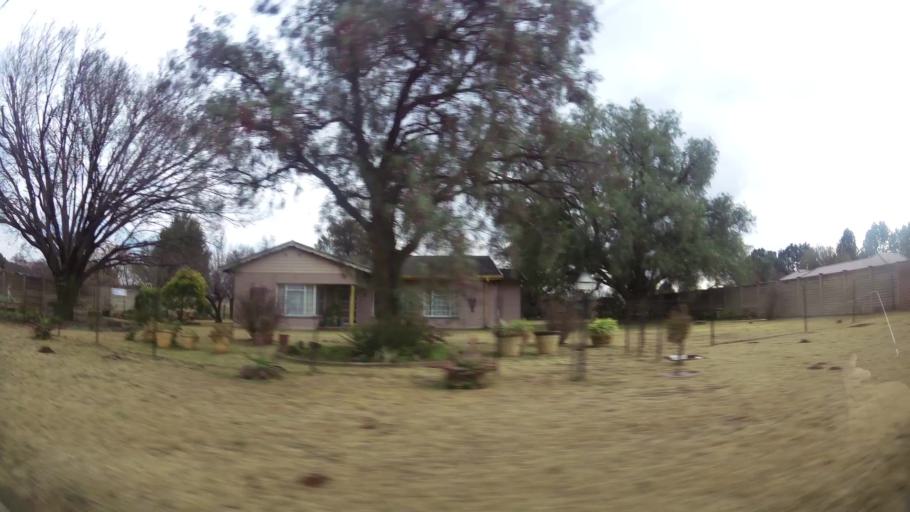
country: ZA
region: Gauteng
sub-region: Sedibeng District Municipality
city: Meyerton
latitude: -26.5861
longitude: 28.0011
